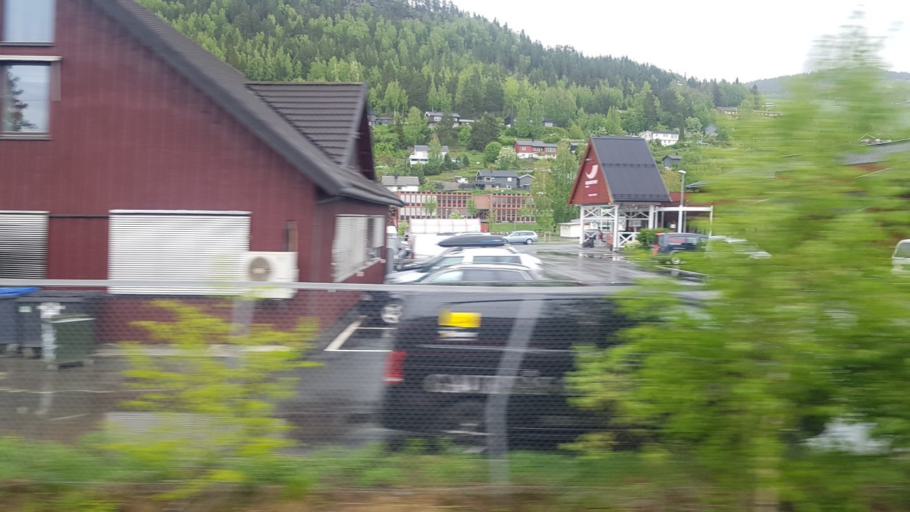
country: NO
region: Oppland
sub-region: Nord-Fron
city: Vinstra
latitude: 61.5826
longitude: 9.7615
